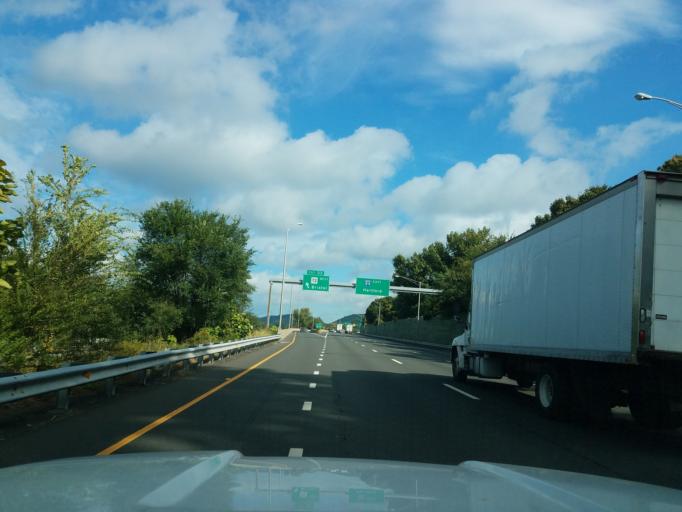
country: US
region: Connecticut
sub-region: Hartford County
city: Plainville
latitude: 41.6647
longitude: -72.8467
